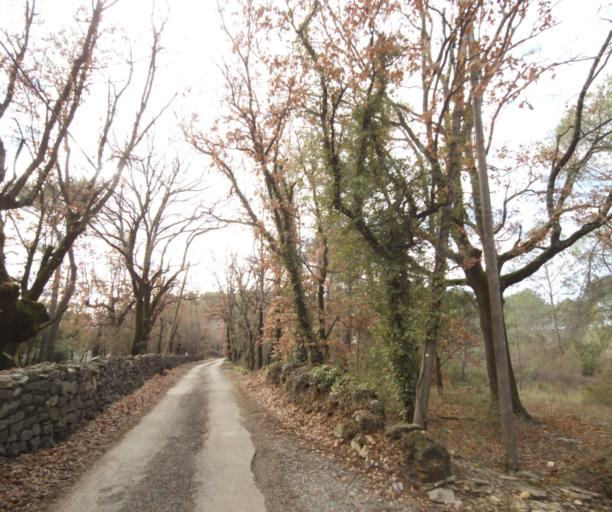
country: FR
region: Provence-Alpes-Cote d'Azur
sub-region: Departement du Var
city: Trans-en-Provence
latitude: 43.5188
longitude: 6.5004
